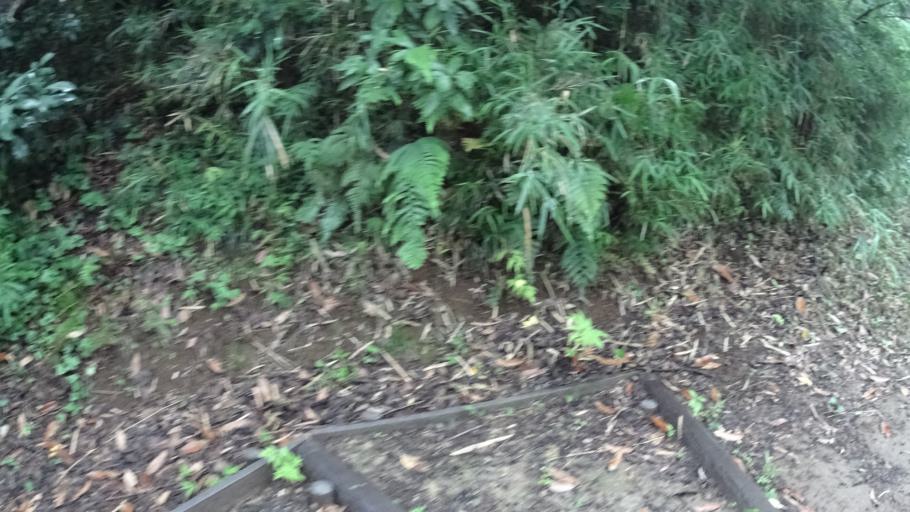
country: JP
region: Kanagawa
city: Zushi
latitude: 35.3518
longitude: 139.6169
